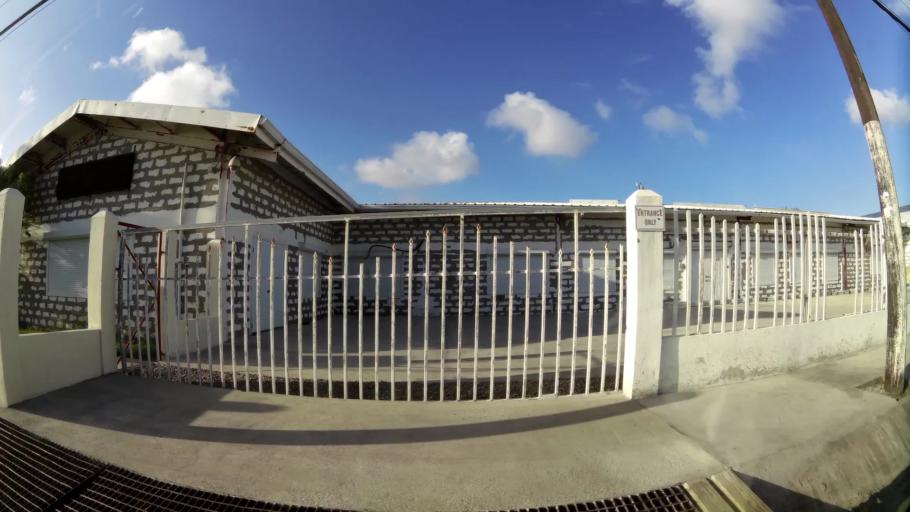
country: KN
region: Saint George Basseterre
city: Basseterre
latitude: 17.2945
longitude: -62.7116
